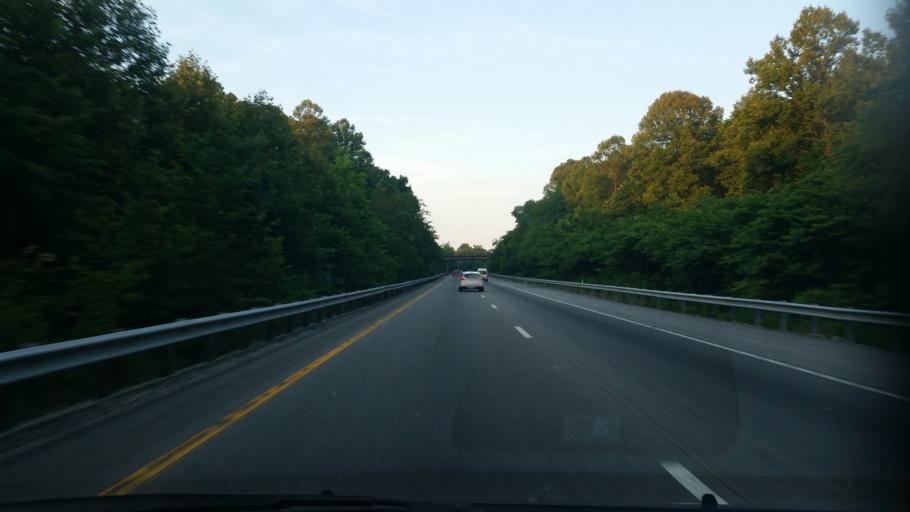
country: US
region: Tennessee
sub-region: Putnam County
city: Algood
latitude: 36.1424
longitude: -85.3774
